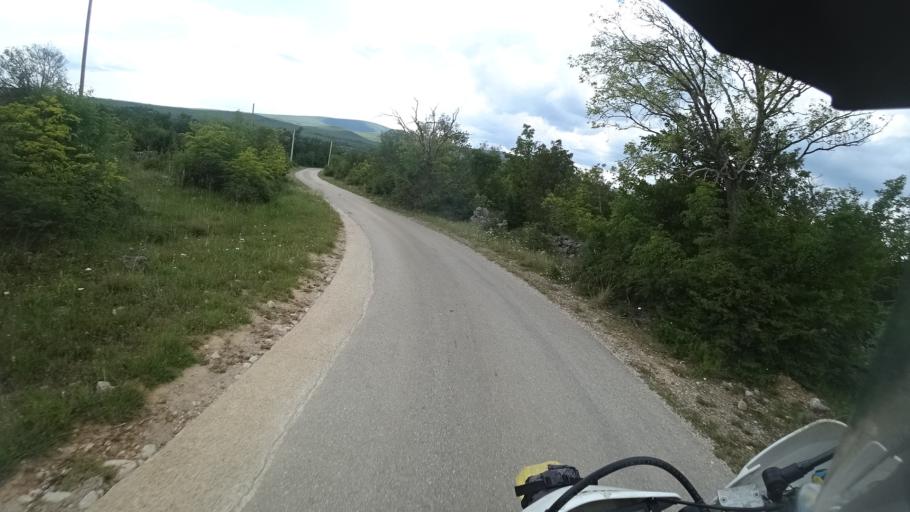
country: HR
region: Sibensko-Kniniska
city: Kistanje
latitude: 44.1076
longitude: 15.9475
